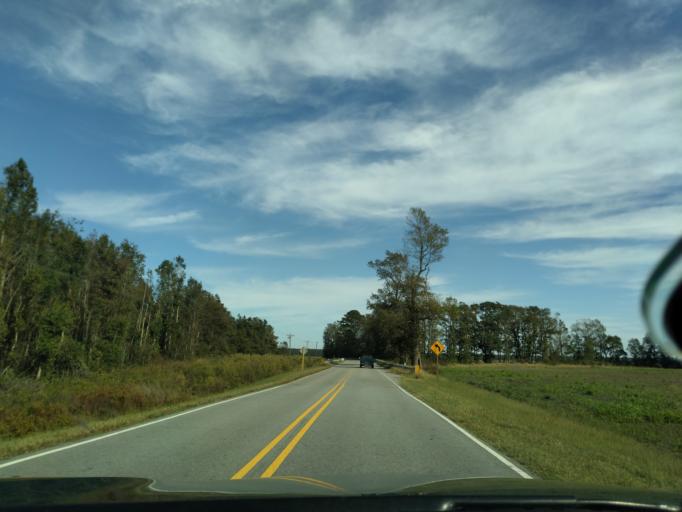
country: US
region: North Carolina
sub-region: Beaufort County
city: Belhaven
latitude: 35.6218
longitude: -76.6391
